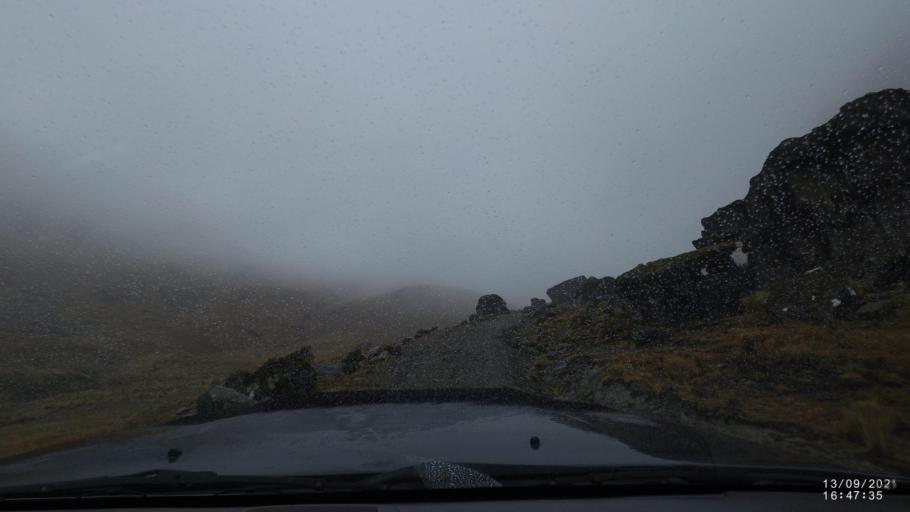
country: BO
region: Cochabamba
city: Colomi
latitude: -17.2976
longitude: -65.7067
